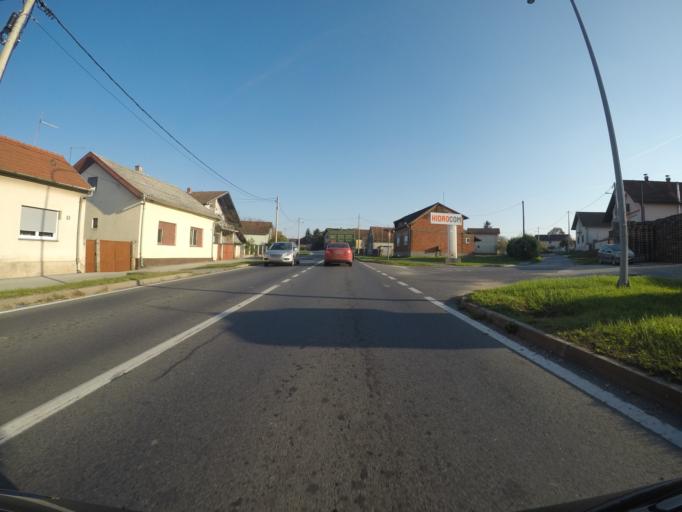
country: HR
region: Virovitick-Podravska
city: Pitomaca
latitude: 45.9444
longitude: 17.2346
